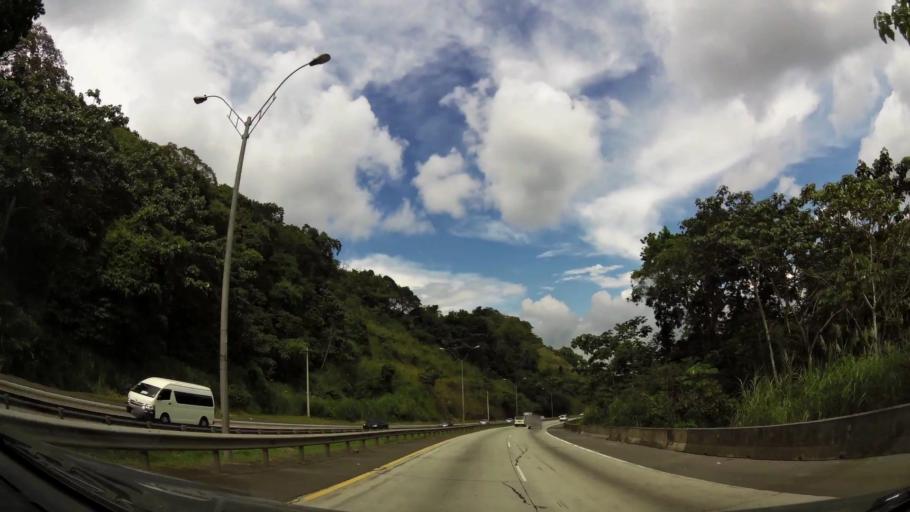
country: PA
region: Panama
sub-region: Distrito de Panama
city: Paraiso
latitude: 9.0080
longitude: -79.6486
